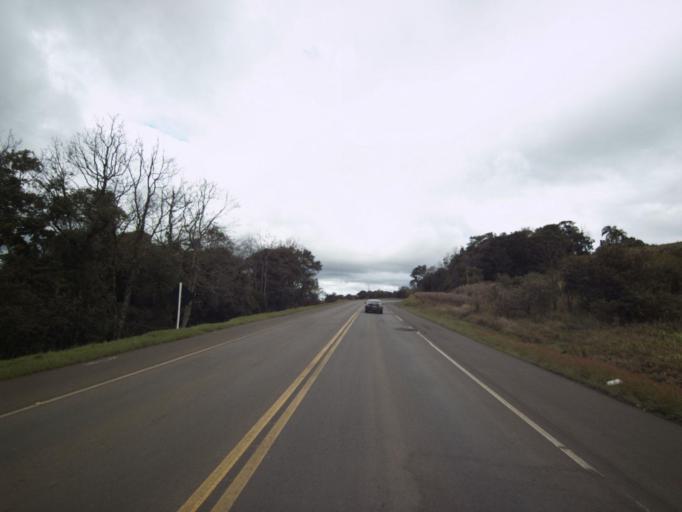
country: BR
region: Santa Catarina
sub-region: Concordia
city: Concordia
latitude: -27.2587
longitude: -51.9542
